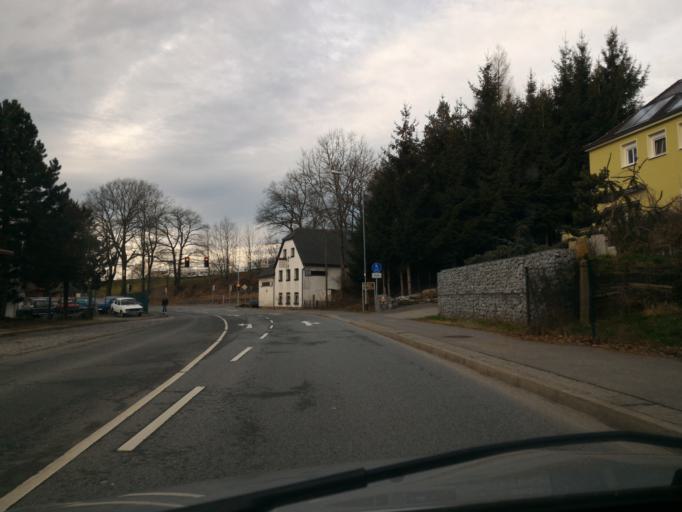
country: DE
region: Saxony
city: Frankenthal
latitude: 51.1151
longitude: 14.1459
